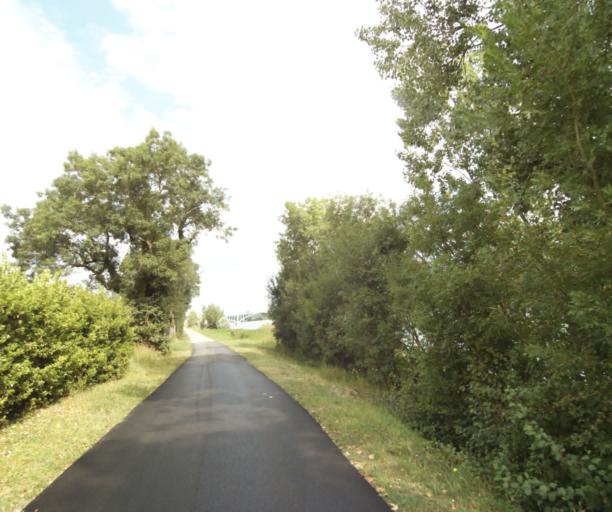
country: FR
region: Bourgogne
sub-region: Departement de Saone-et-Loire
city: Tournus
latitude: 46.5510
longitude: 4.9200
